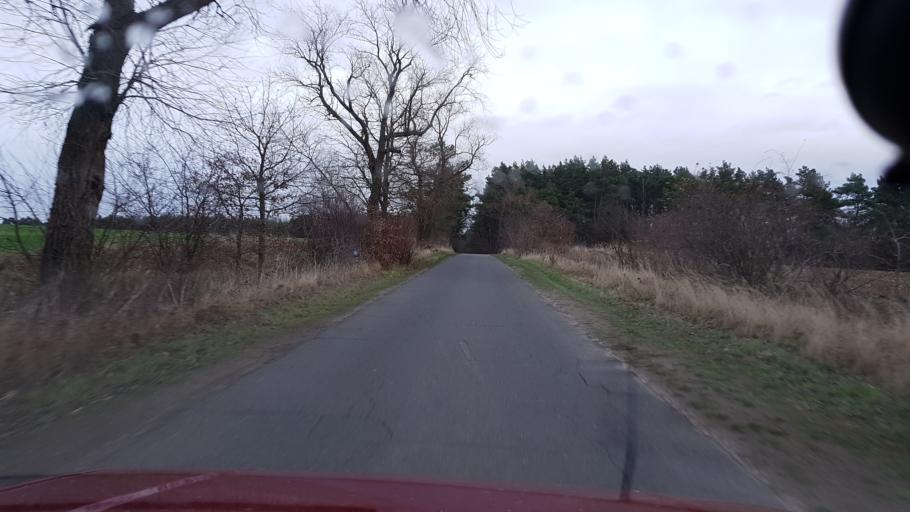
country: PL
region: West Pomeranian Voivodeship
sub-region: Powiat stargardzki
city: Stargard Szczecinski
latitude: 53.3258
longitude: 15.1073
